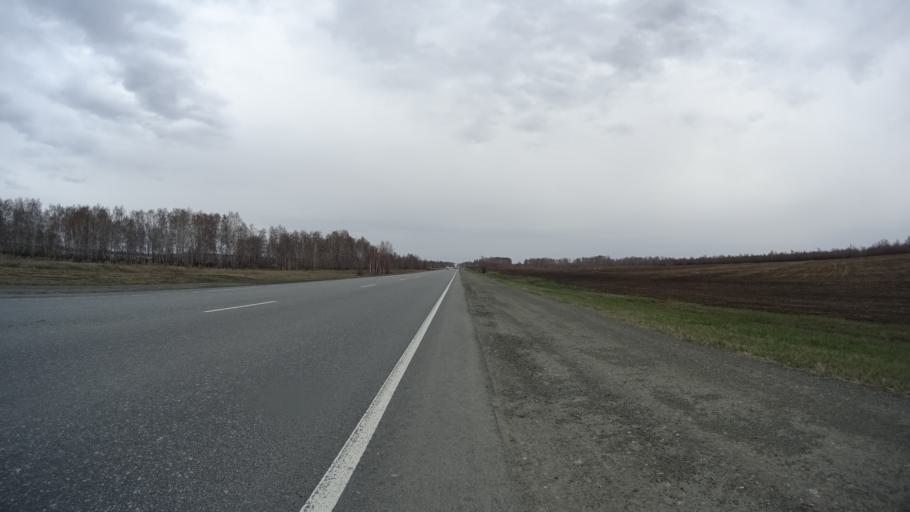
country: RU
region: Chelyabinsk
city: Krasnogorskiy
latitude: 54.6607
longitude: 61.2550
